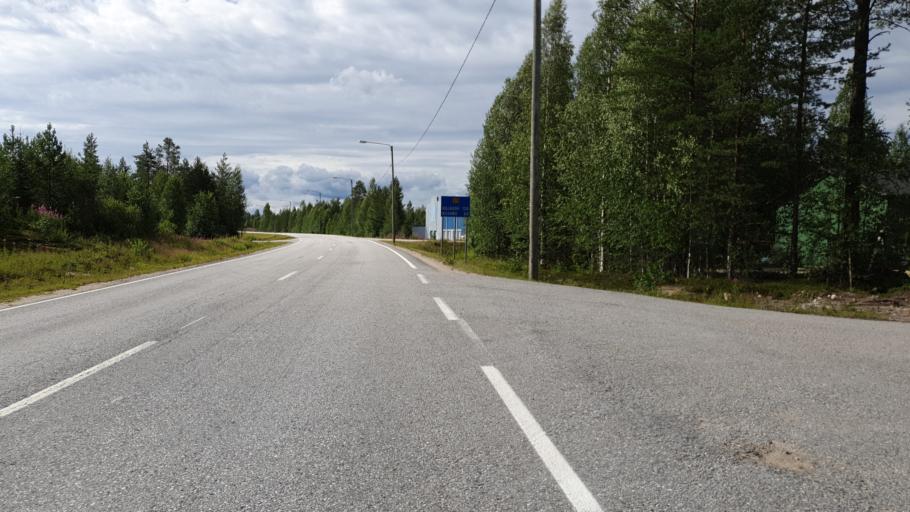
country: FI
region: Kainuu
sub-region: Kehys-Kainuu
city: Kuhmo
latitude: 64.5361
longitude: 29.9445
